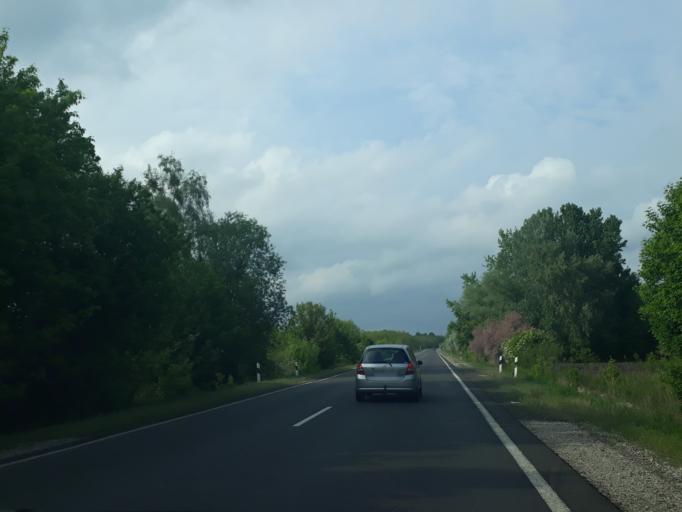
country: HU
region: Szabolcs-Szatmar-Bereg
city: Nyirtass
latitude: 48.0922
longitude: 21.9871
